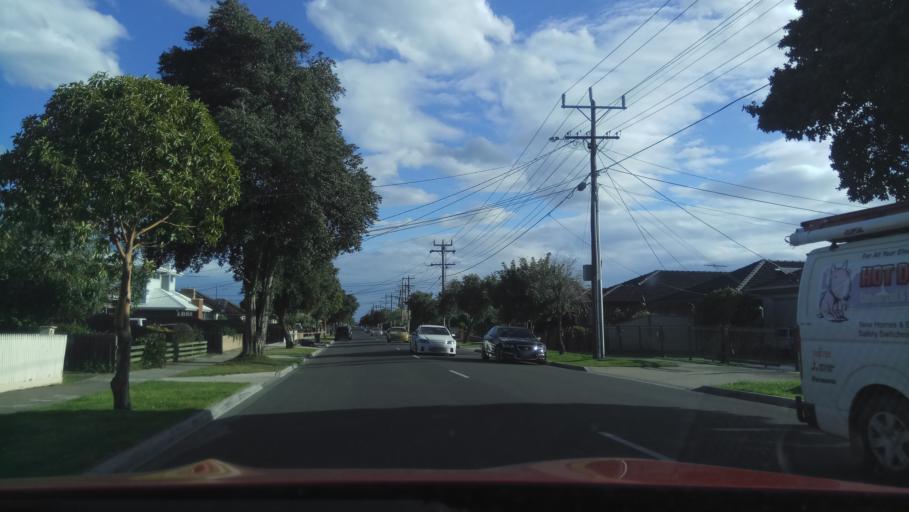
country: AU
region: Victoria
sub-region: Hobsons Bay
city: Altona North
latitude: -37.8290
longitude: 144.8437
